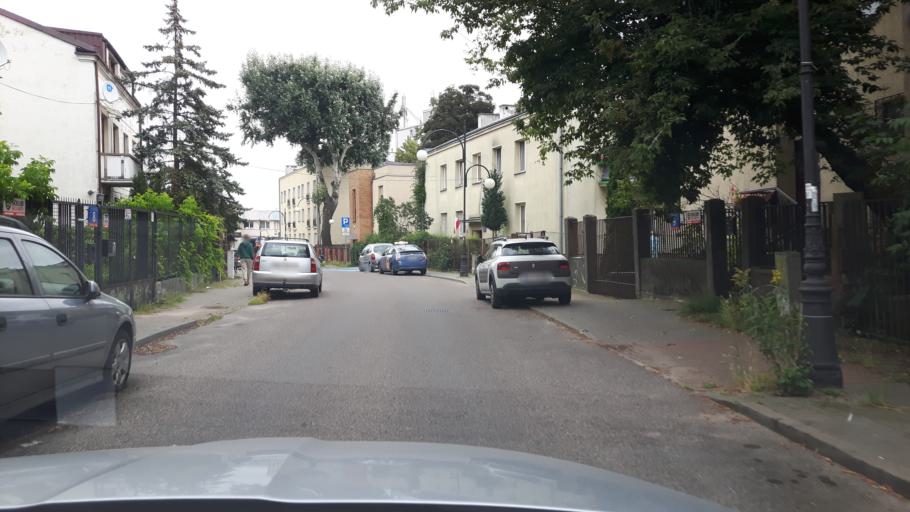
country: PL
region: Masovian Voivodeship
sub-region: Warszawa
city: Zoliborz
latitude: 52.2741
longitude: 20.9775
